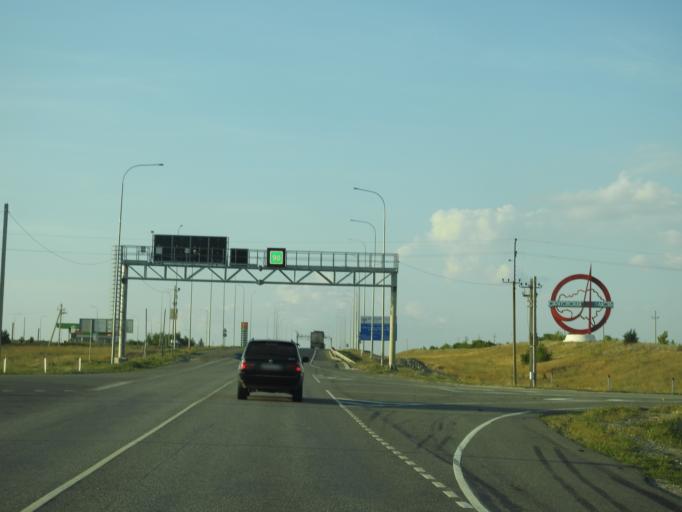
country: RU
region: Saratov
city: Kamenskiy
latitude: 50.6068
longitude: 45.4755
